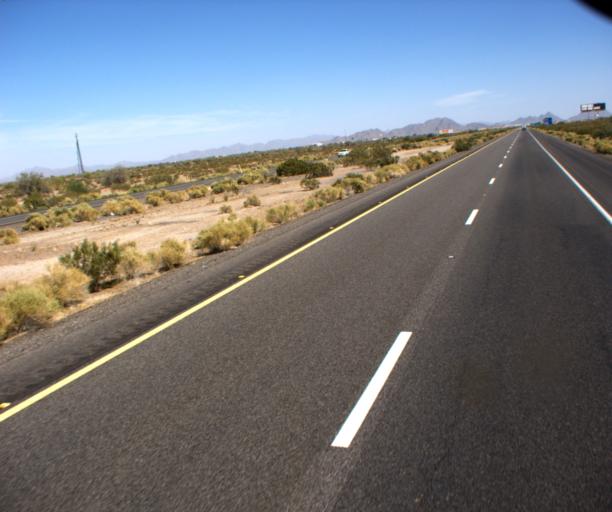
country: US
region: Arizona
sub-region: Maricopa County
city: Gila Bend
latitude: 32.9300
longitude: -112.6936
